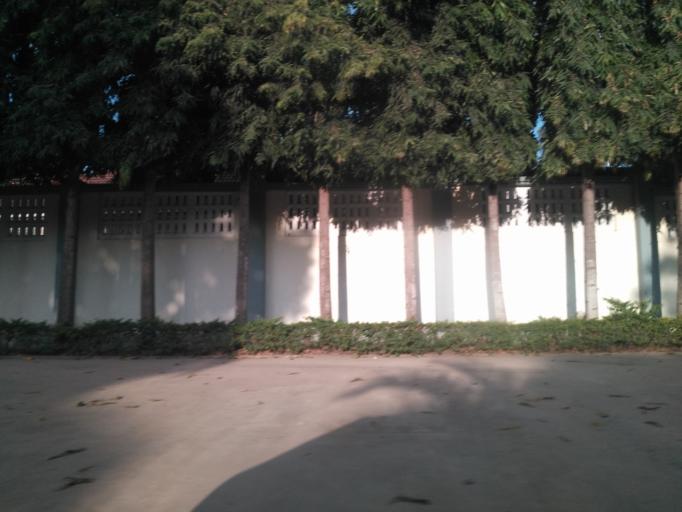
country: TZ
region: Dar es Salaam
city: Magomeni
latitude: -6.7849
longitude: 39.2724
